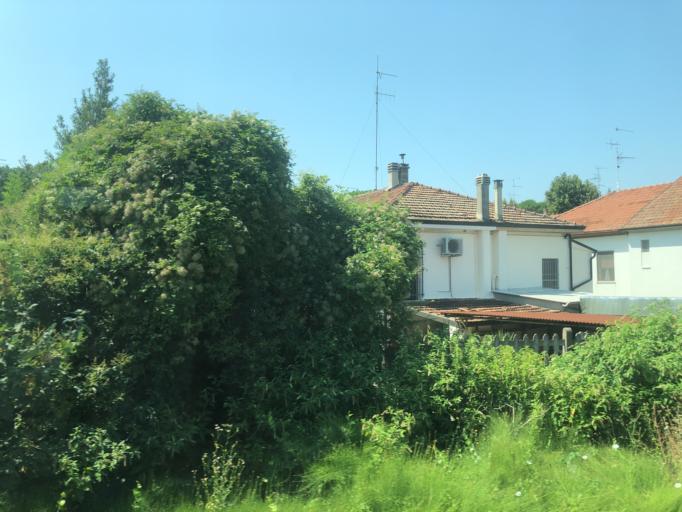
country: IT
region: Emilia-Romagna
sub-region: Forli-Cesena
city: Cesena
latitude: 44.1426
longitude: 12.2584
